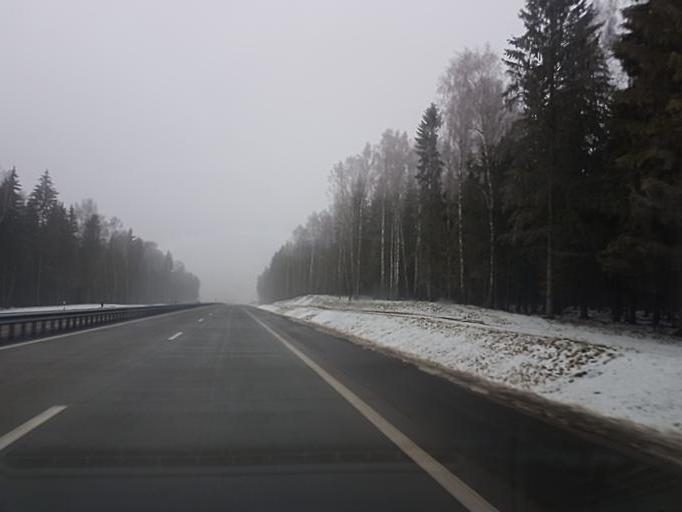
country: BY
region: Minsk
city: Atolina
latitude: 53.7207
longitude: 27.4309
